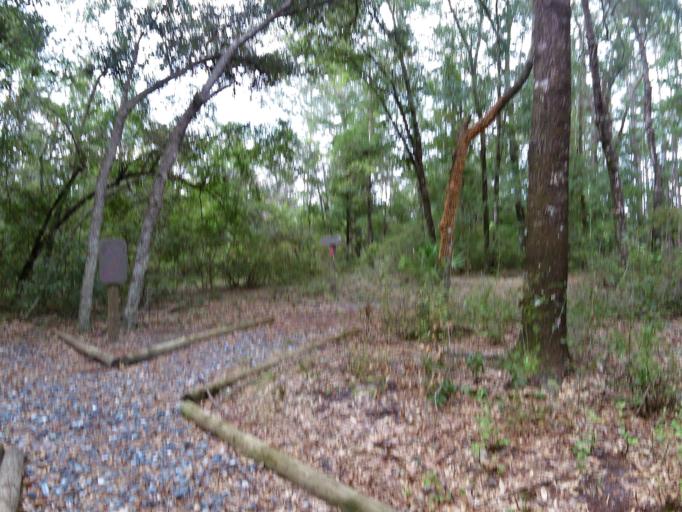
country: US
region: Florida
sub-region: Clay County
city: Middleburg
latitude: 30.1377
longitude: -81.9554
